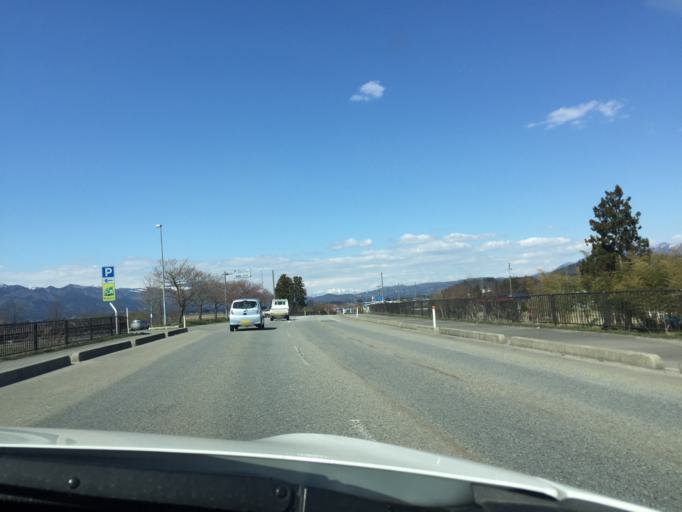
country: JP
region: Yamagata
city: Nagai
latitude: 38.1366
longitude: 140.0555
